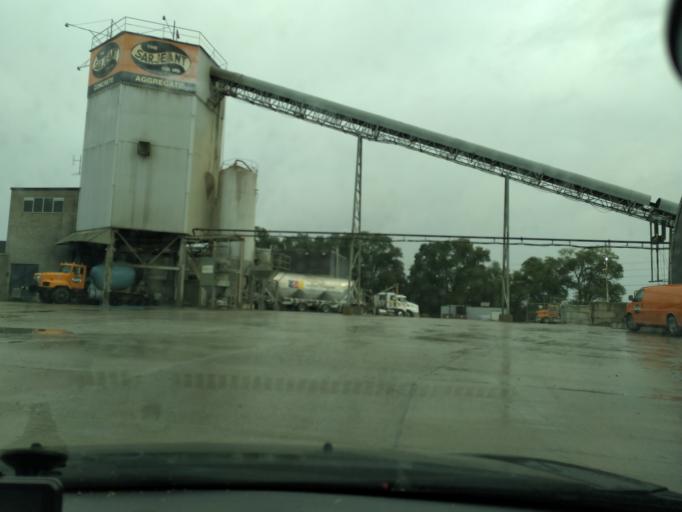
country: CA
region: Ontario
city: Barrie
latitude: 44.3756
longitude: -79.7148
